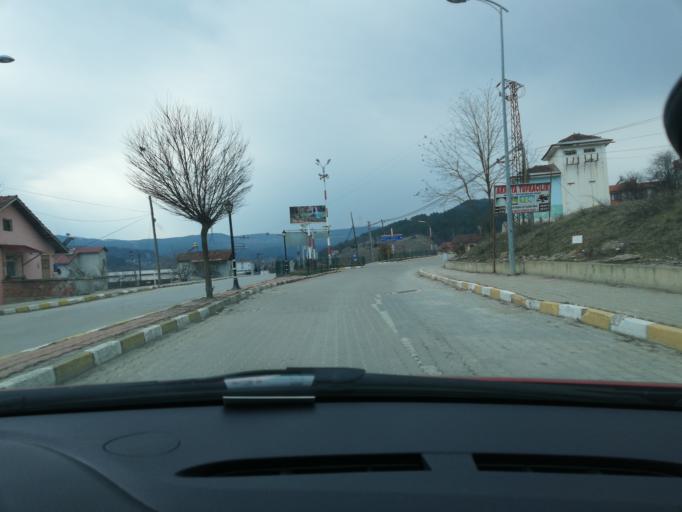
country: TR
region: Kastamonu
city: Pinarbasi
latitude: 41.6016
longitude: 33.1072
